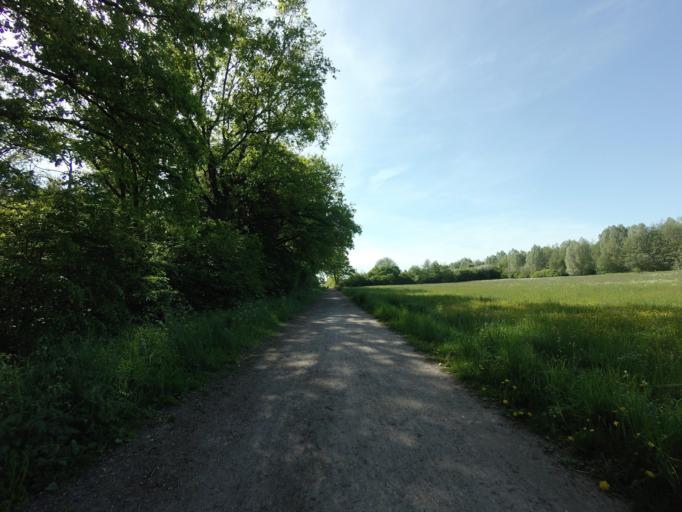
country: DE
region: Lower Saxony
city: Cremlingen
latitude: 52.2920
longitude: 10.6145
